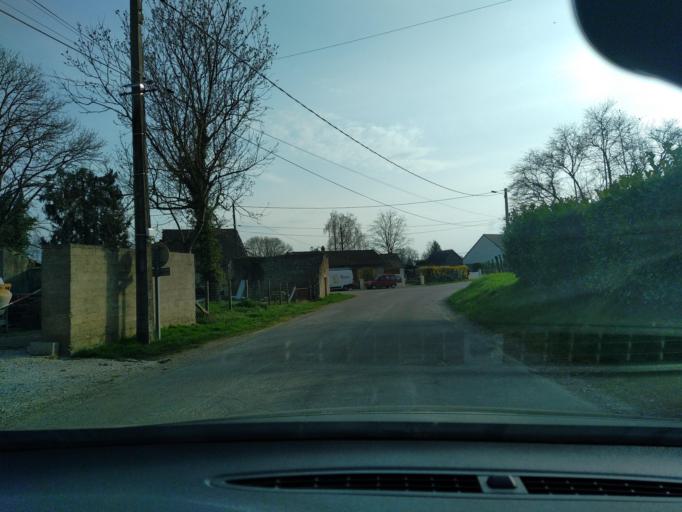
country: FR
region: Franche-Comte
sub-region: Departement du Jura
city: Chaussin
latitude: 46.9909
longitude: 5.4664
